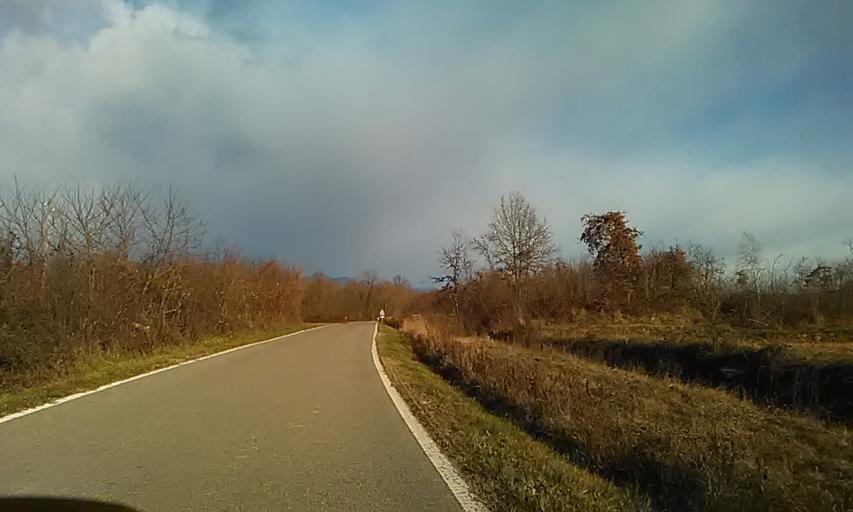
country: IT
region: Piedmont
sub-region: Provincia di Biella
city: Brusnengo
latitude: 45.5694
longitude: 8.2724
